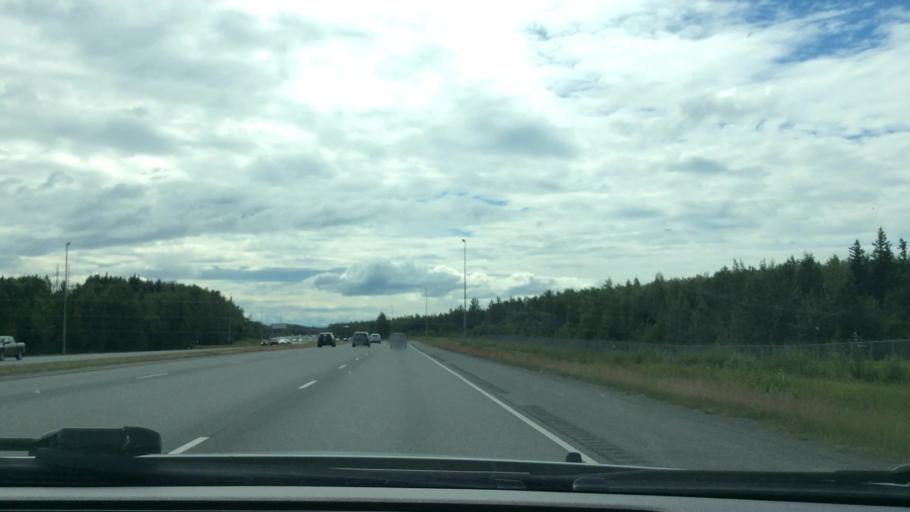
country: US
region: Alaska
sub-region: Anchorage Municipality
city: Elmendorf Air Force Base
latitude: 61.2479
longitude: -149.6741
